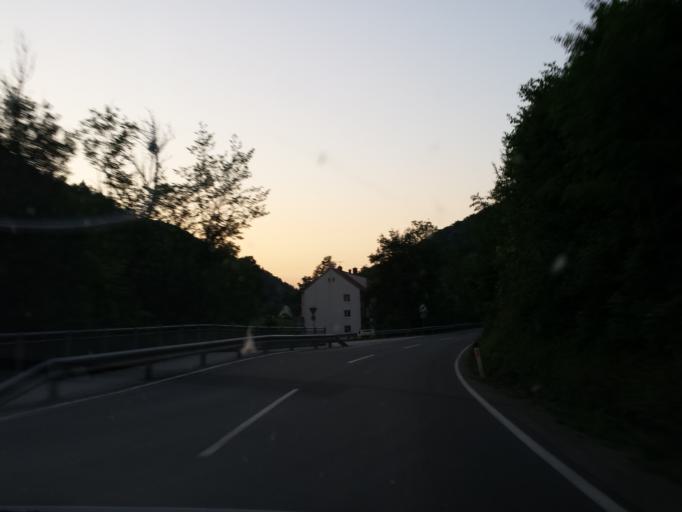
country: AT
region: Lower Austria
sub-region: Politischer Bezirk Lilienfeld
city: Hainfeld
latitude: 48.0154
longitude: 15.7765
